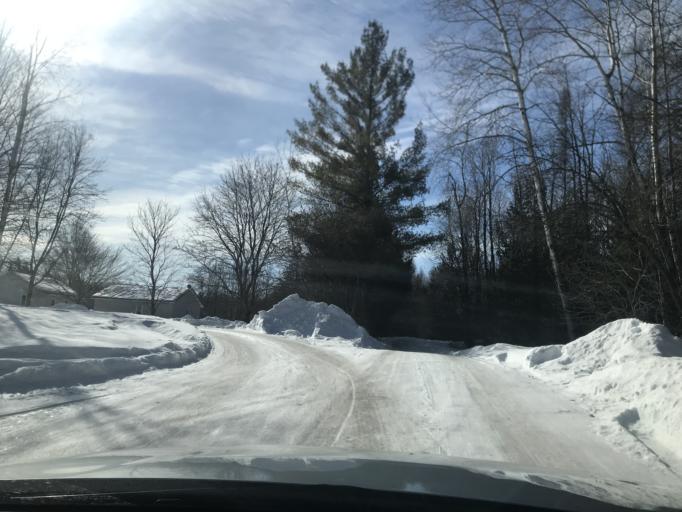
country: US
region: Wisconsin
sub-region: Oconto County
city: Gillett
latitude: 44.9578
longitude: -88.2755
